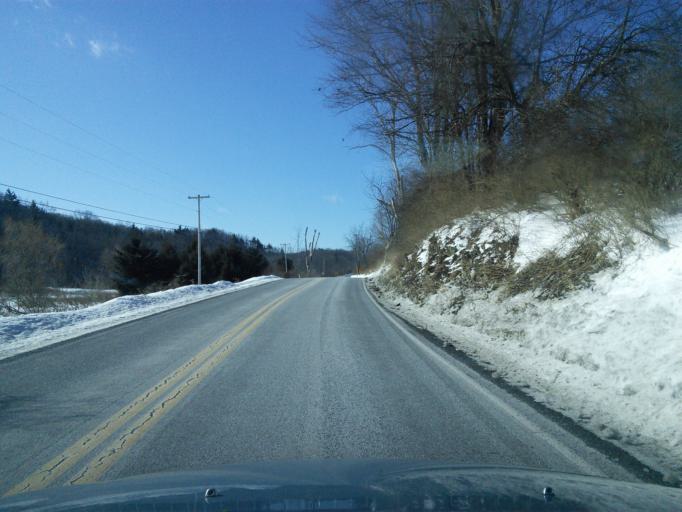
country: US
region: Pennsylvania
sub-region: Centre County
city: Park Forest Village
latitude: 40.8424
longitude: -77.9170
